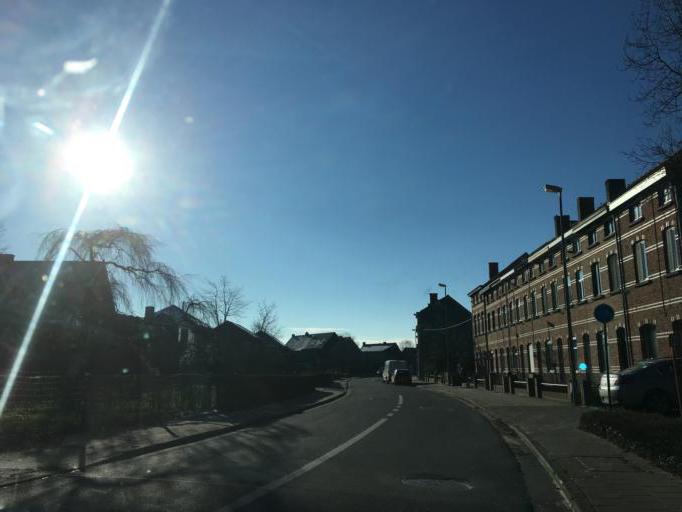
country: BE
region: Flanders
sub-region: Provincie Oost-Vlaanderen
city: Waarschoot
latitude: 51.1560
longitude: 3.6159
